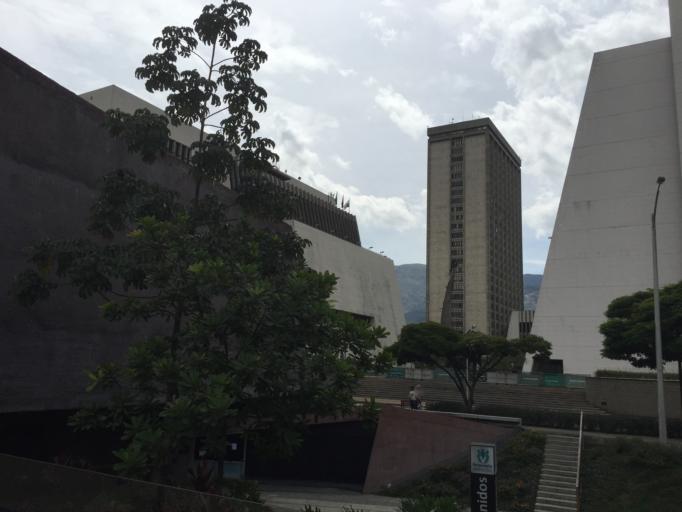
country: CO
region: Antioquia
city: Medellin
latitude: 6.2440
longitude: -75.5748
